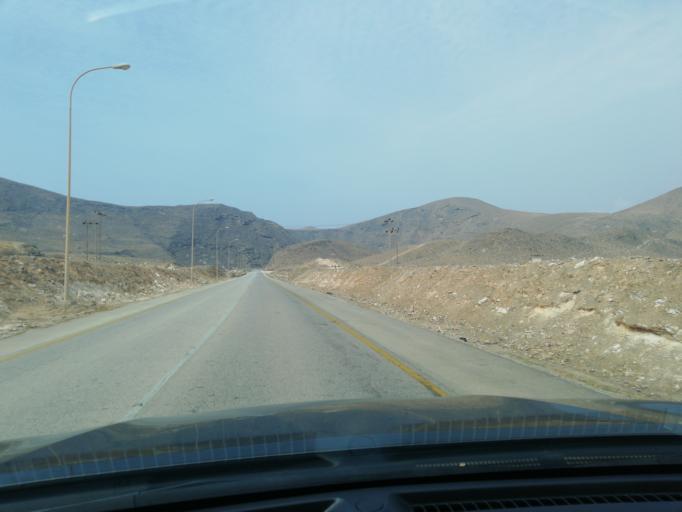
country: OM
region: Zufar
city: Salalah
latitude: 16.9046
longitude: 53.8217
